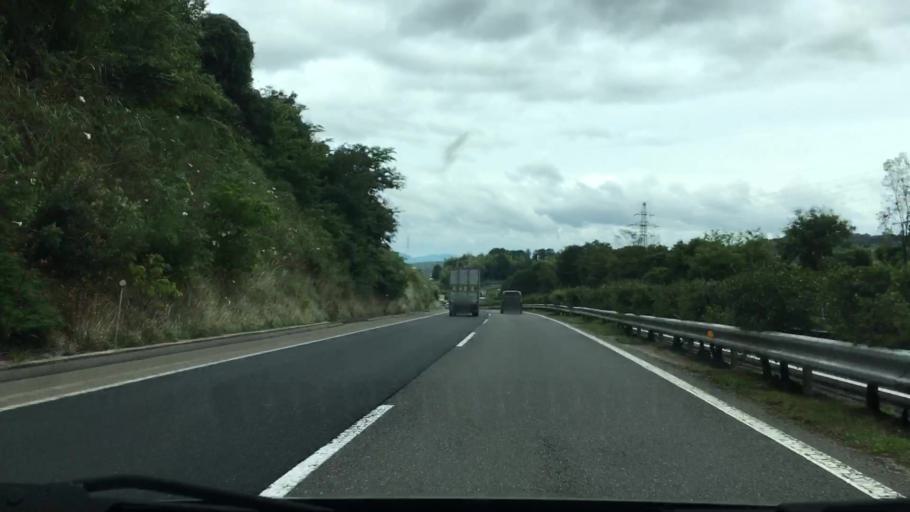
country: JP
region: Okayama
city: Tsuyama
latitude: 35.0650
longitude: 133.9690
